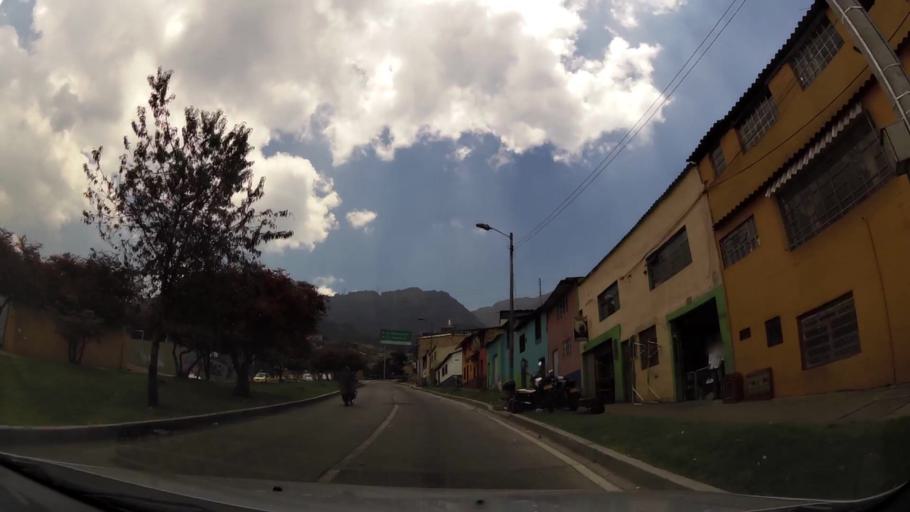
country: CO
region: Bogota D.C.
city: Bogota
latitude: 4.5919
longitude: -74.0716
